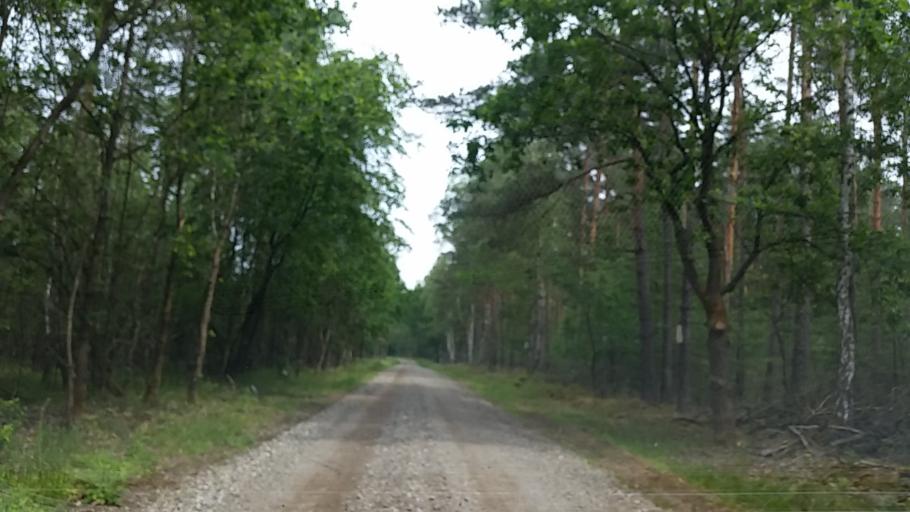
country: DE
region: Lower Saxony
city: Dedelstorf
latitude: 52.6919
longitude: 10.5321
